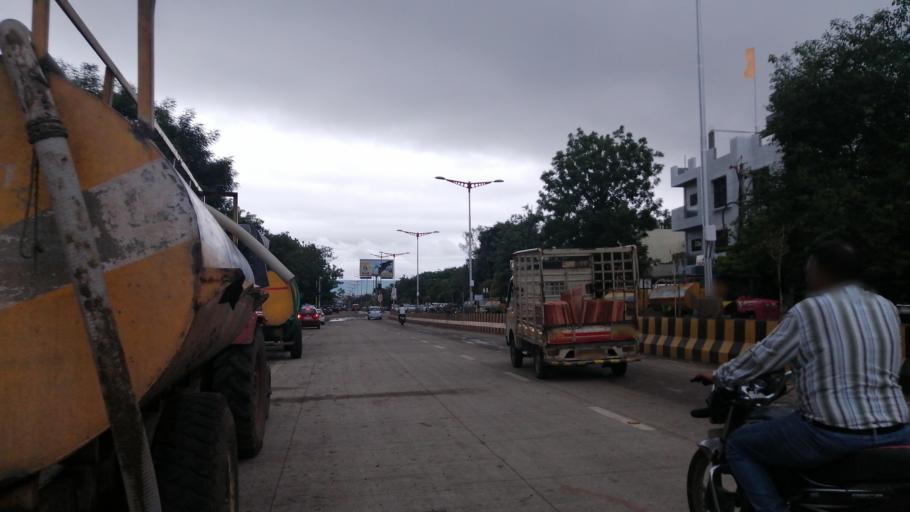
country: IN
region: Maharashtra
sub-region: Aurangabad Division
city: Aurangabad
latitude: 19.8793
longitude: 75.3715
